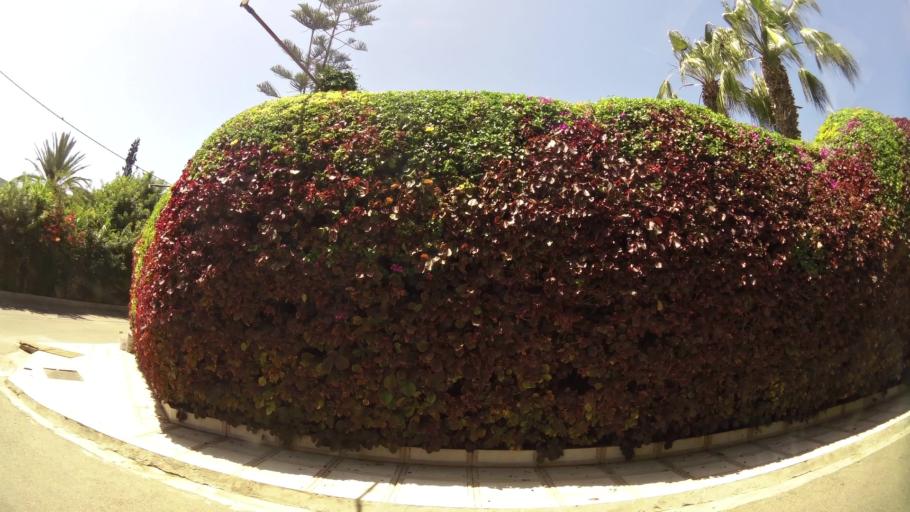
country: MA
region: Souss-Massa-Draa
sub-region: Agadir-Ida-ou-Tnan
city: Agadir
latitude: 30.4289
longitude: -9.5997
